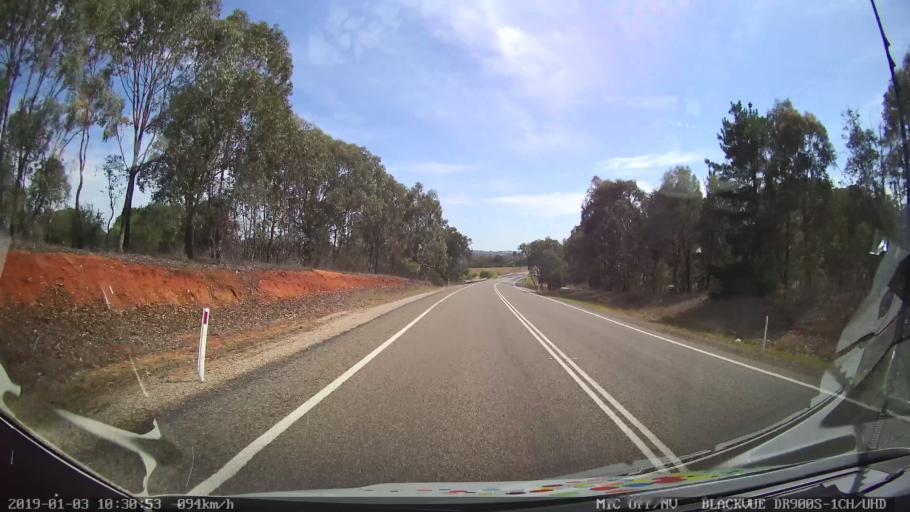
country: AU
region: New South Wales
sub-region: Young
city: Young
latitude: -34.3570
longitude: 148.2723
